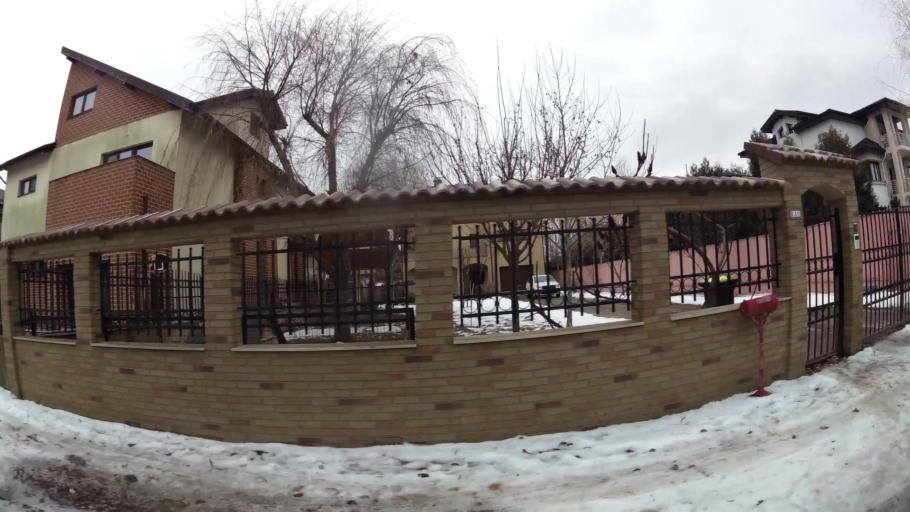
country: RO
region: Ilfov
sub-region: Comuna Otopeni
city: Otopeni
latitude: 44.5545
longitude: 26.1039
